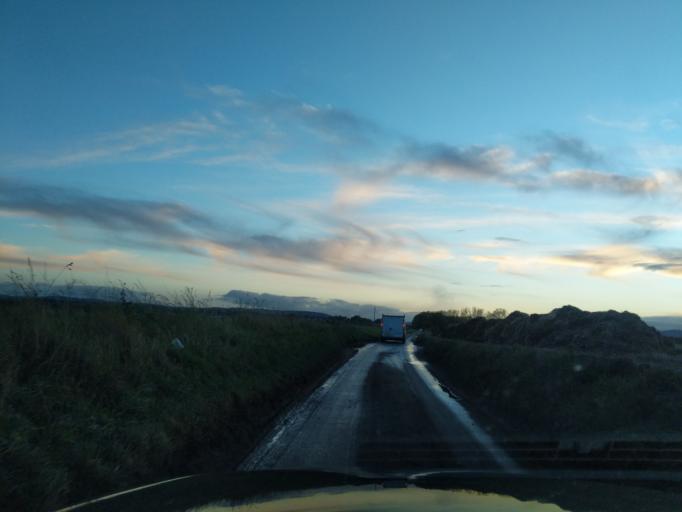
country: GB
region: Scotland
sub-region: Fife
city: Leuchars
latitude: 56.3972
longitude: -2.8655
